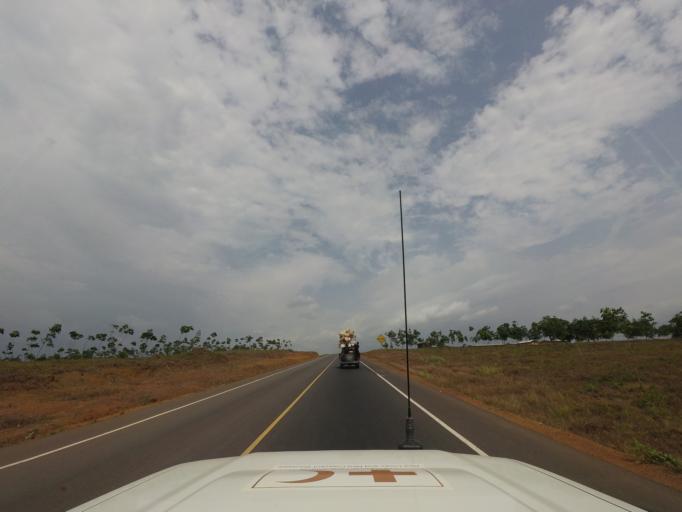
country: LR
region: Margibi
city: Kakata
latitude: 6.4492
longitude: -10.4434
